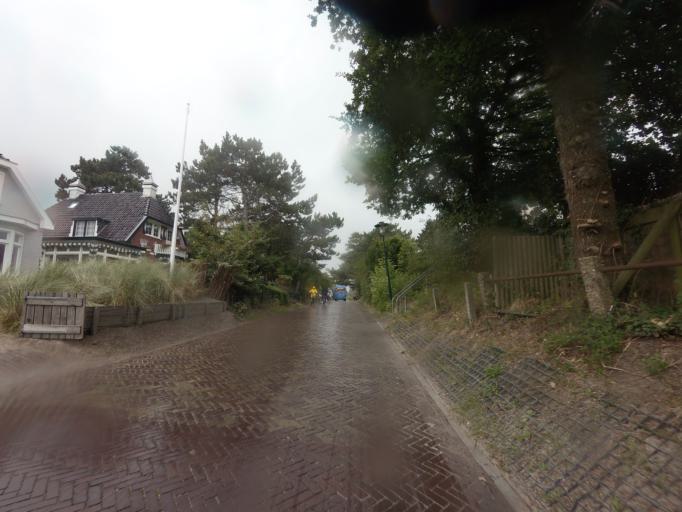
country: NL
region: Friesland
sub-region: Gemeente Schiermonnikoog
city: Schiermonnikoog
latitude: 53.4809
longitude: 6.1610
